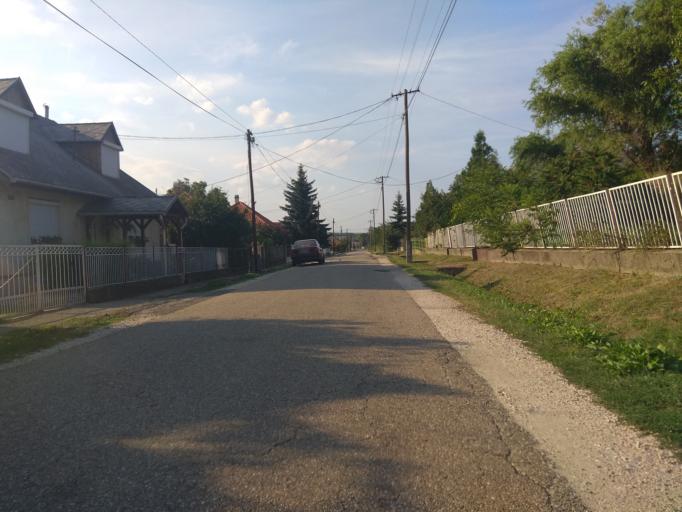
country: HU
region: Borsod-Abauj-Zemplen
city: Harsany
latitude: 47.9191
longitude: 20.7399
